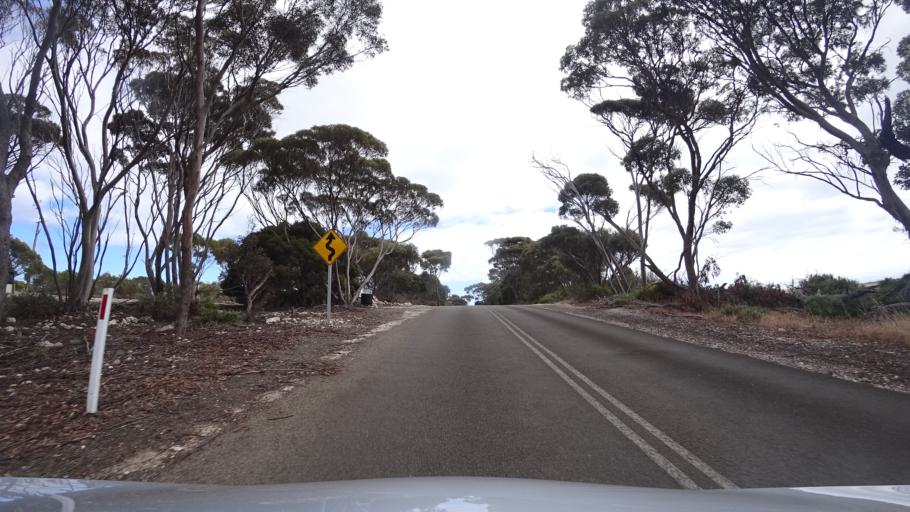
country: AU
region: South Australia
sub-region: Kangaroo Island
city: Kingscote
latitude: -35.6046
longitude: 137.5217
